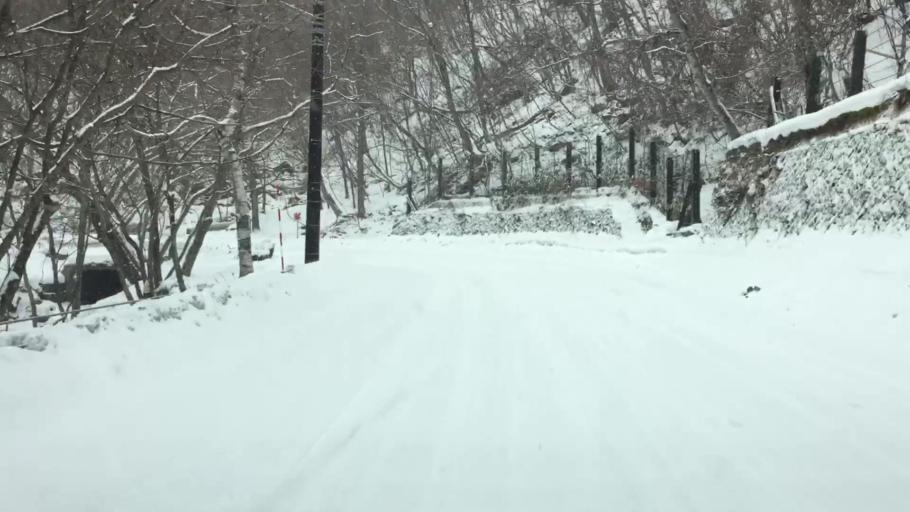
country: JP
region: Tochigi
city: Imaichi
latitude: 36.9070
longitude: 139.7409
